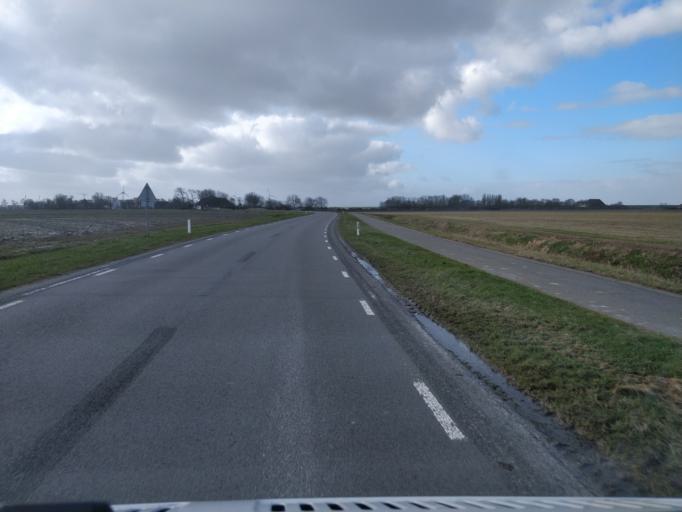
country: NL
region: Friesland
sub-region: Gemeente Franekeradeel
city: Sexbierum
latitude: 53.2060
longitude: 5.4593
